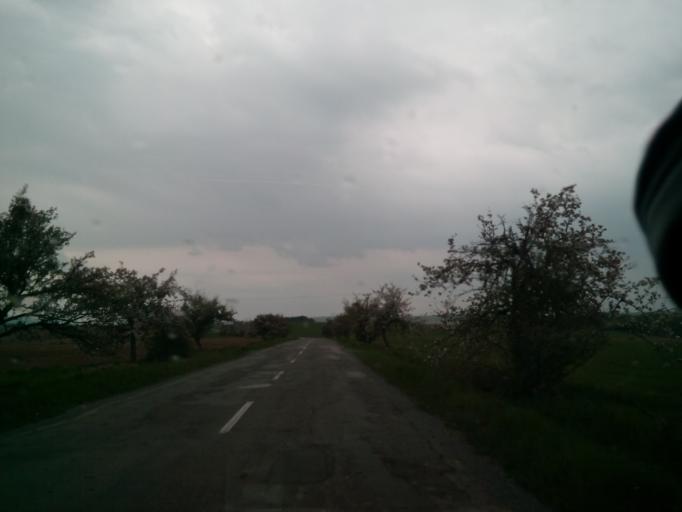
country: SK
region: Kosicky
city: Secovce
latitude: 48.7699
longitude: 21.4721
